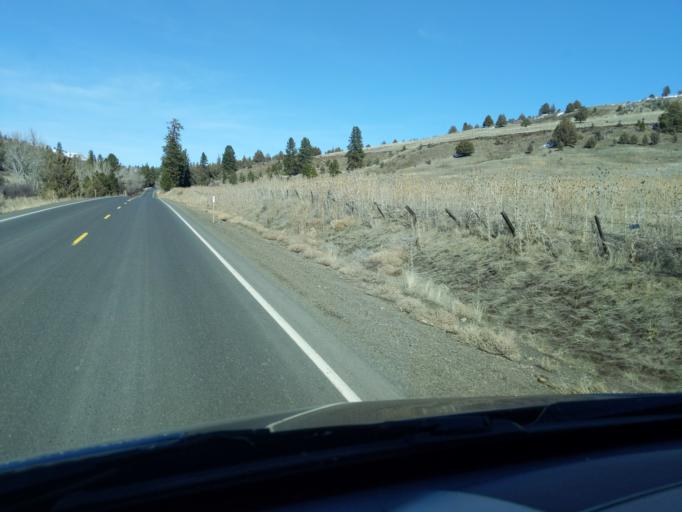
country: US
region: Oregon
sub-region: Grant County
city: John Day
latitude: 44.8580
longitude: -119.0282
